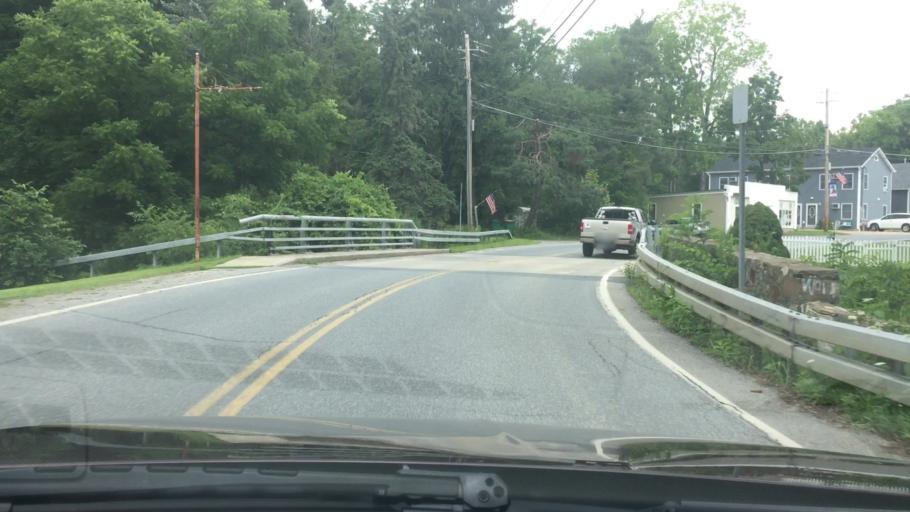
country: US
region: New York
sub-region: Dutchess County
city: Pawling
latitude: 41.6079
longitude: -73.6816
